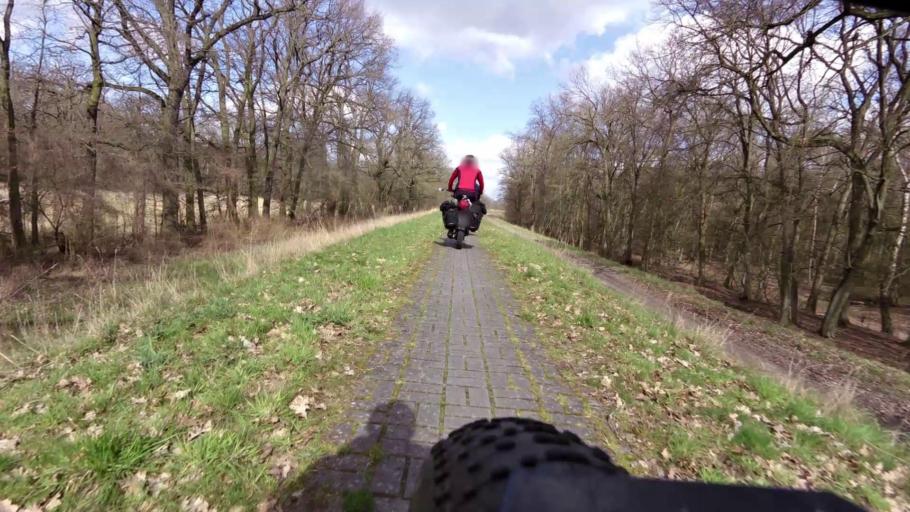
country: DE
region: Brandenburg
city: Lebus
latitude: 52.3953
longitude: 14.5406
